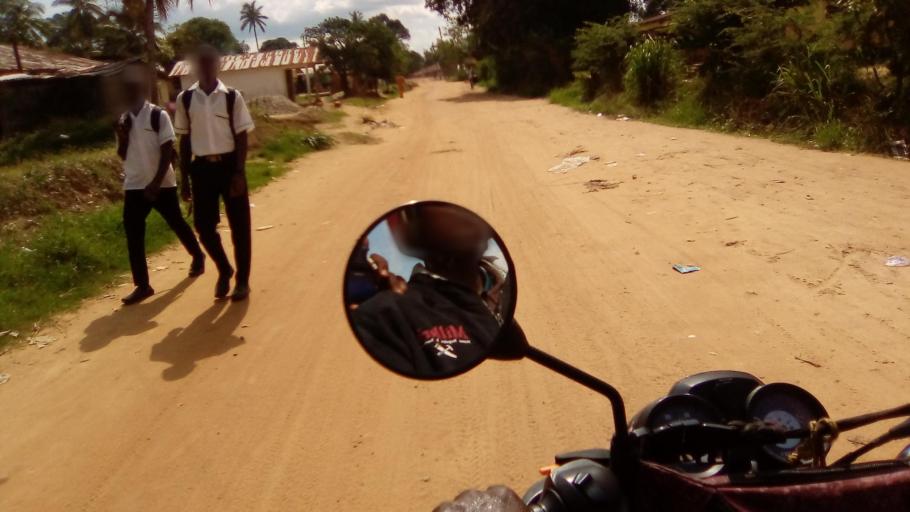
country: SL
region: Southern Province
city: Bo
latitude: 7.9515
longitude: -11.7262
